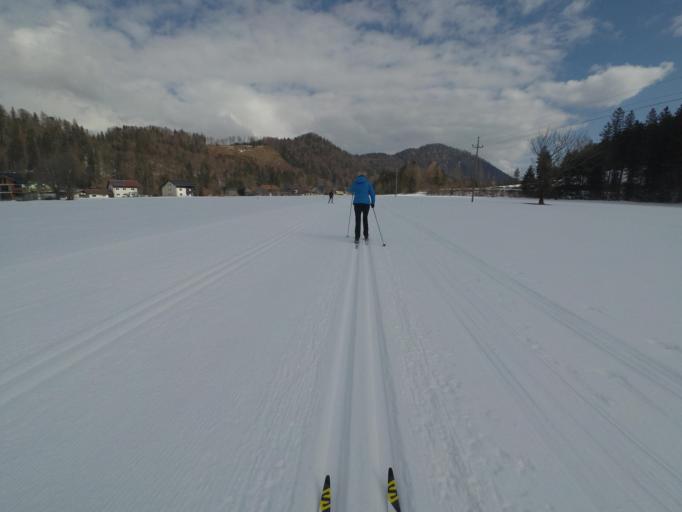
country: AT
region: Salzburg
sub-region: Politischer Bezirk Salzburg-Umgebung
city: Fuschl am See
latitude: 47.7733
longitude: 13.2975
